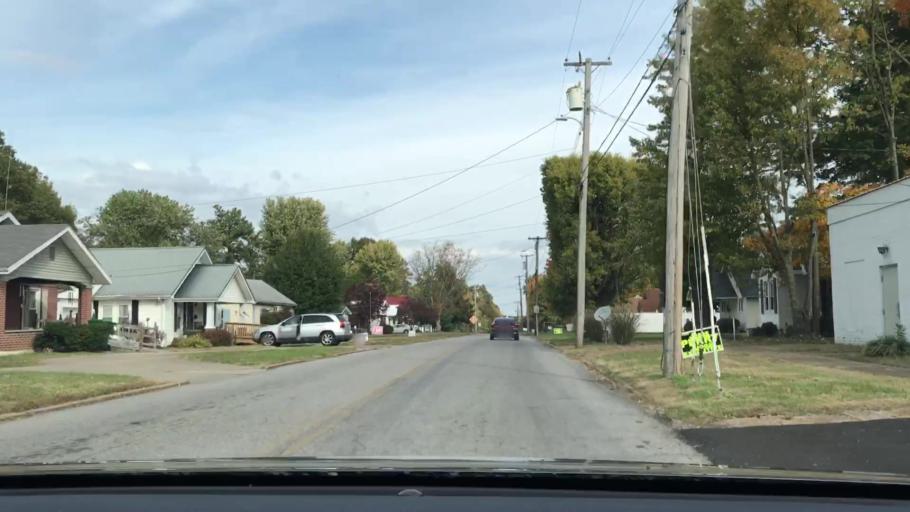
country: US
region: Kentucky
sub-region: Graves County
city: Mayfield
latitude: 36.7420
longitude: -88.6496
